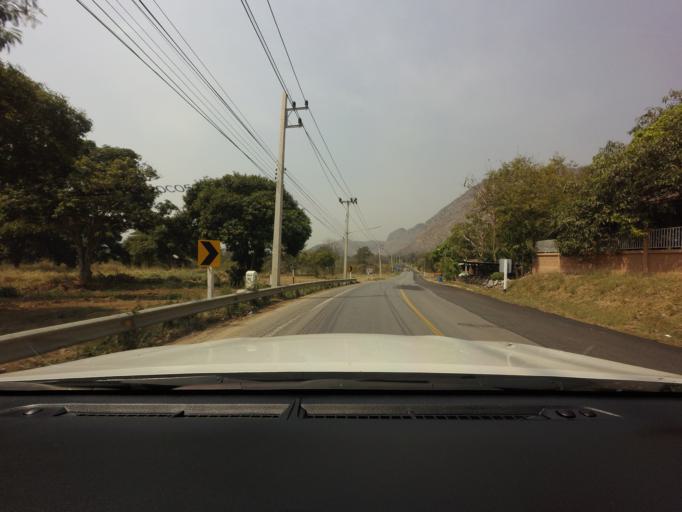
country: TH
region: Sara Buri
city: Muak Lek
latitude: 14.5790
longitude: 101.2610
